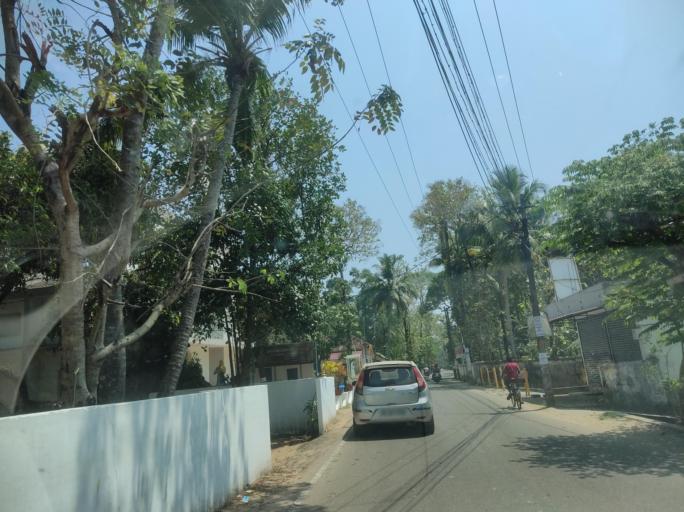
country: IN
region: Kerala
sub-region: Alappuzha
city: Kutiatodu
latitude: 9.8413
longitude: 76.2960
